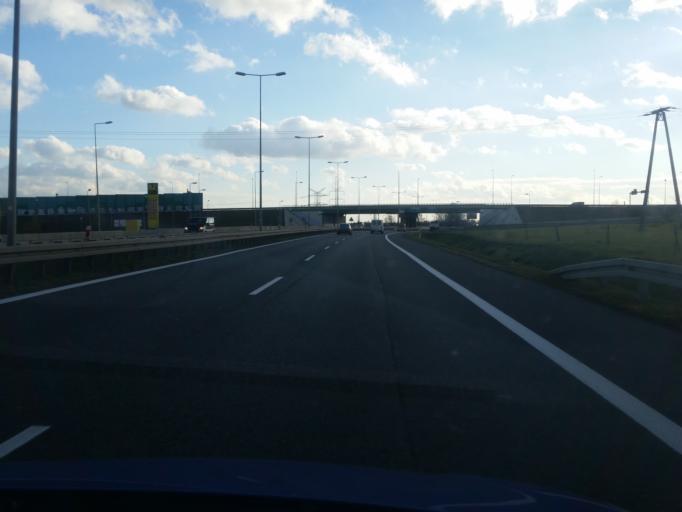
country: PL
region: Silesian Voivodeship
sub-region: Powiat bedzinski
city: Siewierz
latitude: 50.4620
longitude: 19.2313
